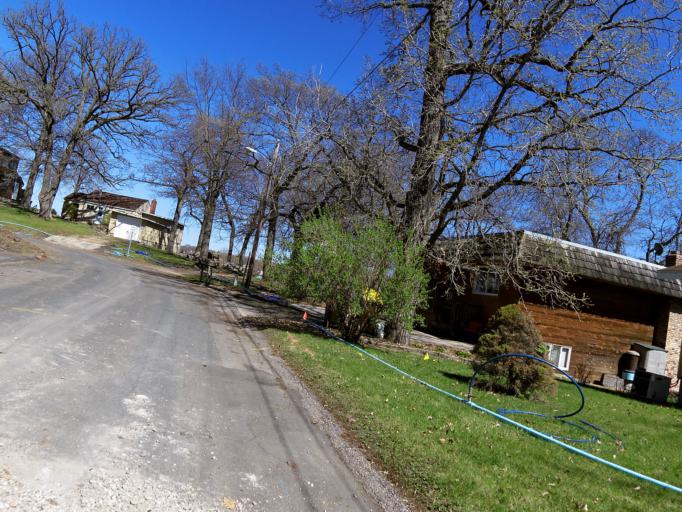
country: US
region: Minnesota
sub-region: Scott County
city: Prior Lake
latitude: 44.7219
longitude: -93.4347
